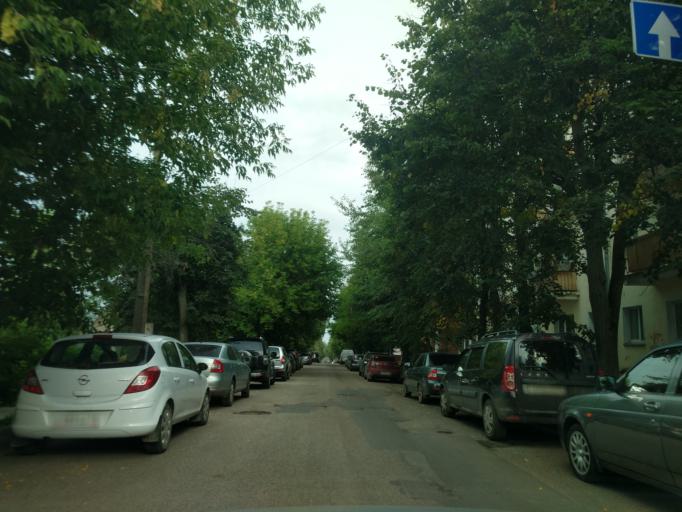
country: RU
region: Kirov
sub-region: Kirovo-Chepetskiy Rayon
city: Kirov
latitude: 58.5962
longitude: 49.6775
